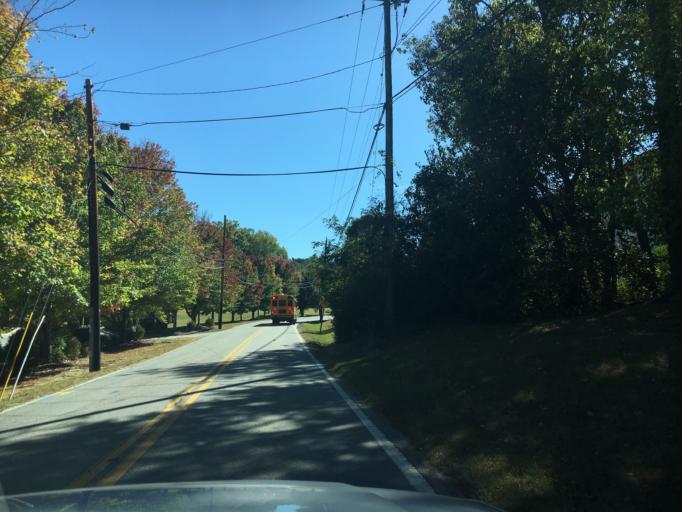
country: US
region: North Carolina
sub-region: Buncombe County
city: Woodfin
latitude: 35.6360
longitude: -82.5753
